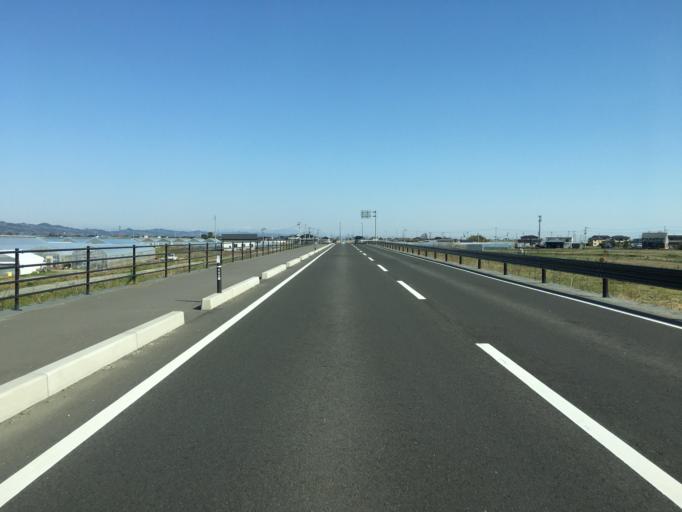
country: JP
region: Miyagi
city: Watari
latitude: 37.9591
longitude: 140.9034
